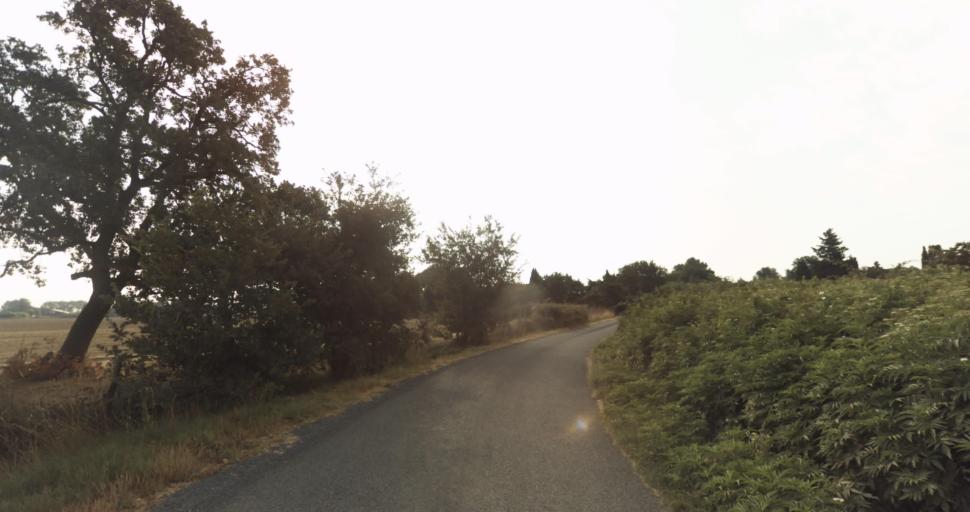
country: FR
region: Languedoc-Roussillon
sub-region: Departement des Pyrenees-Orientales
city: Corneilla-del-Vercol
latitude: 42.6135
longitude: 2.9446
